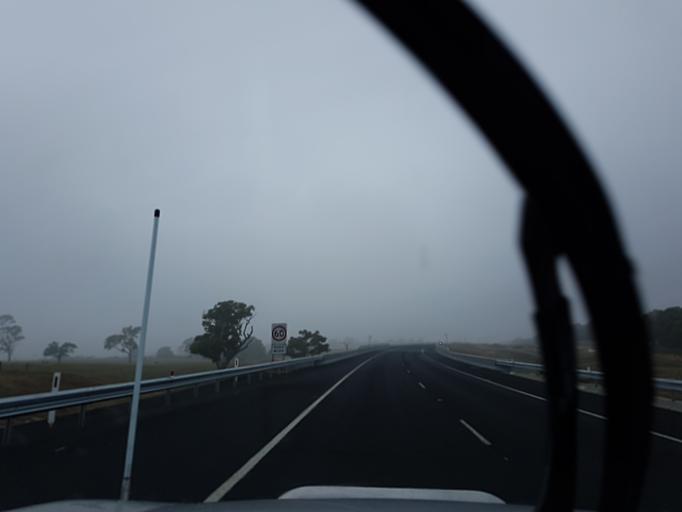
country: AU
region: Victoria
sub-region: Latrobe
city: Traralgon
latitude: -38.1803
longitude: 146.6163
